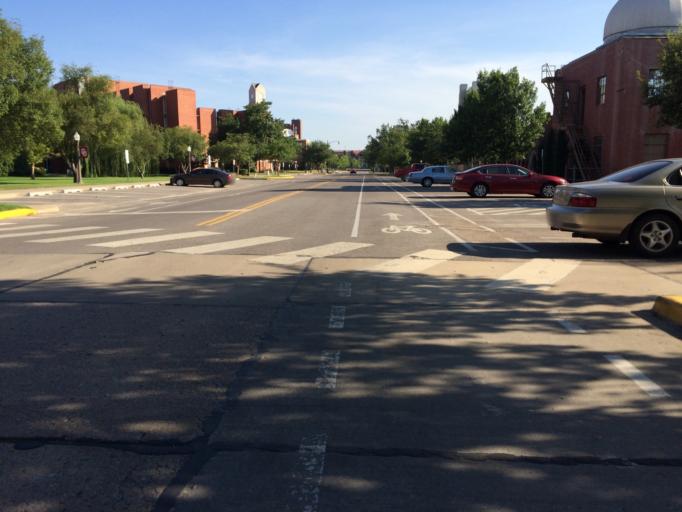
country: US
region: Oklahoma
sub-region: Cleveland County
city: Norman
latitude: 35.2021
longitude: -97.4442
